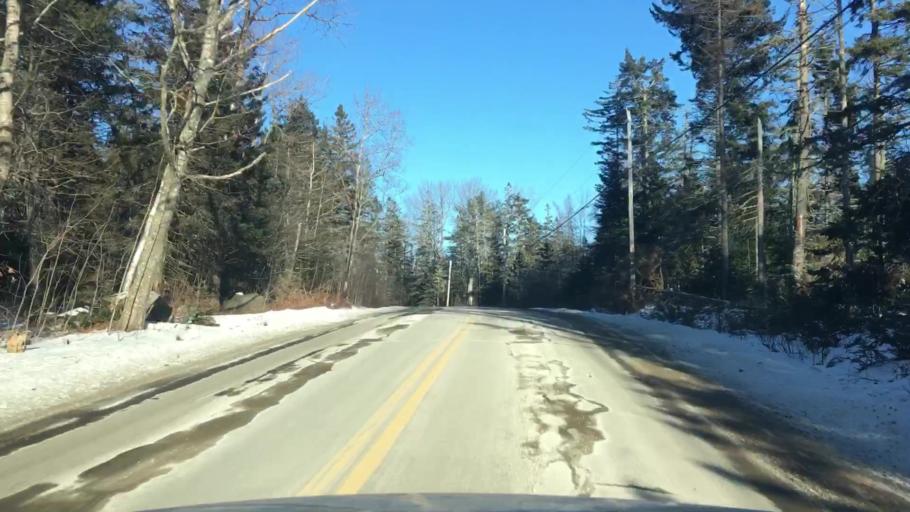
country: US
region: Maine
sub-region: Hancock County
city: Penobscot
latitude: 44.3978
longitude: -68.6994
